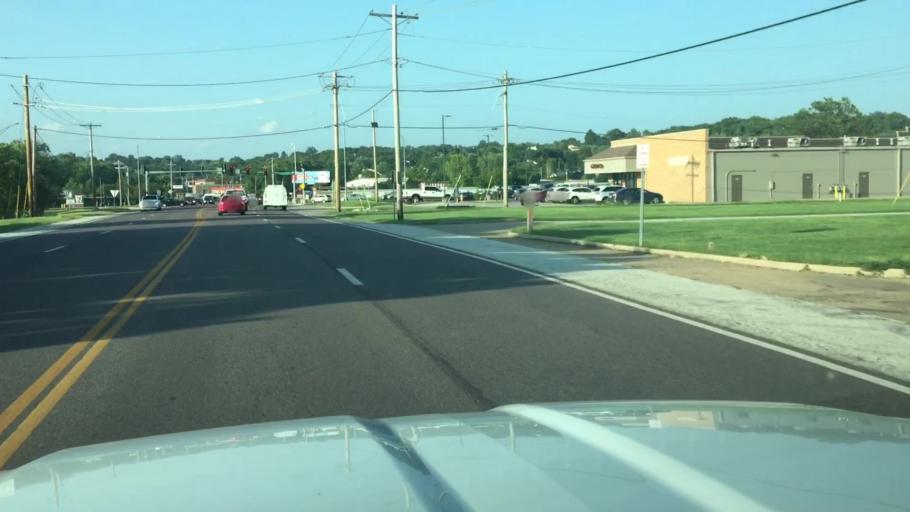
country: US
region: Missouri
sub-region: Jefferson County
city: Arnold
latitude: 38.4634
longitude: -90.3578
